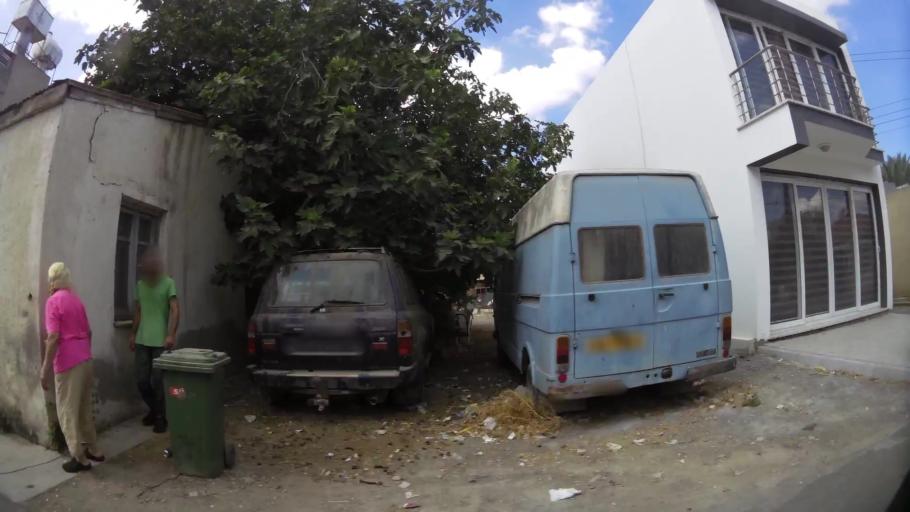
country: CY
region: Lefkosia
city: Nicosia
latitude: 35.2159
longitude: 33.3051
